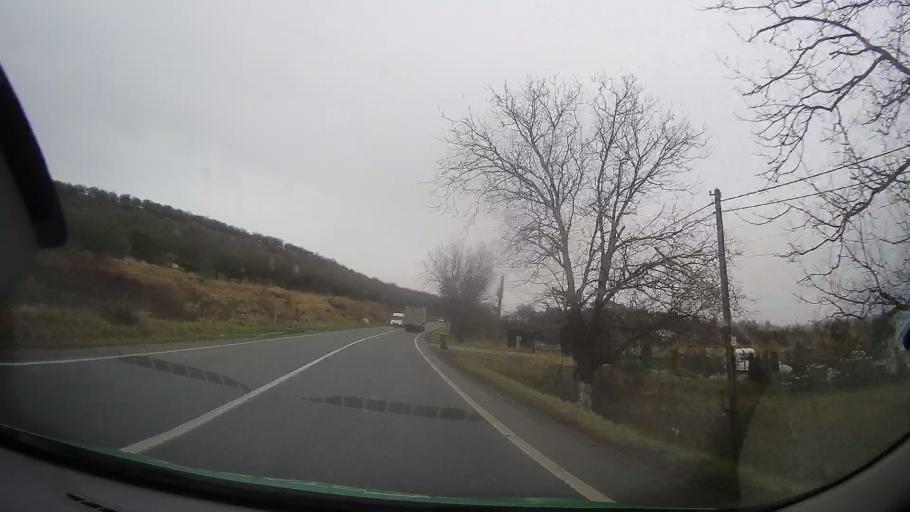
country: RO
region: Mures
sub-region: Comuna Breaza
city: Breaza
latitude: 46.7673
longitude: 24.6587
